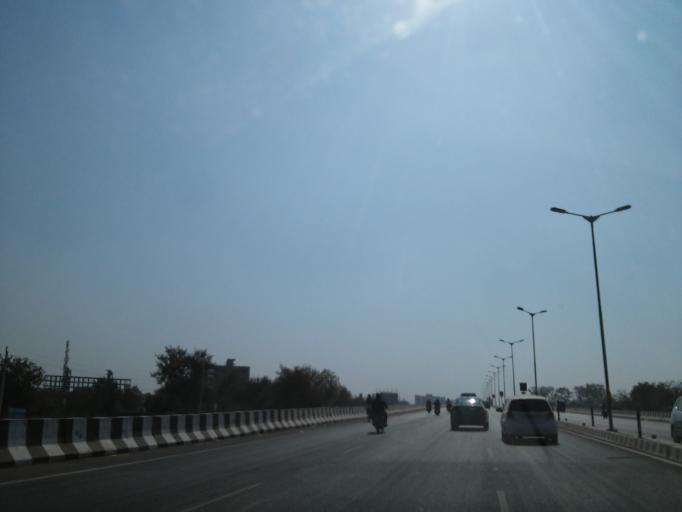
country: IN
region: Gujarat
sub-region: Gandhinagar
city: Adalaj
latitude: 23.1052
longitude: 72.5336
